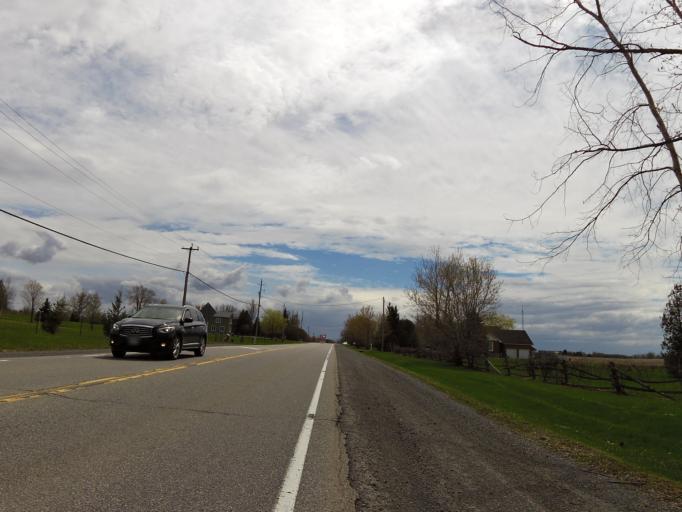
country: CA
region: Ontario
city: Hawkesbury
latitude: 45.5428
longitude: -74.6400
